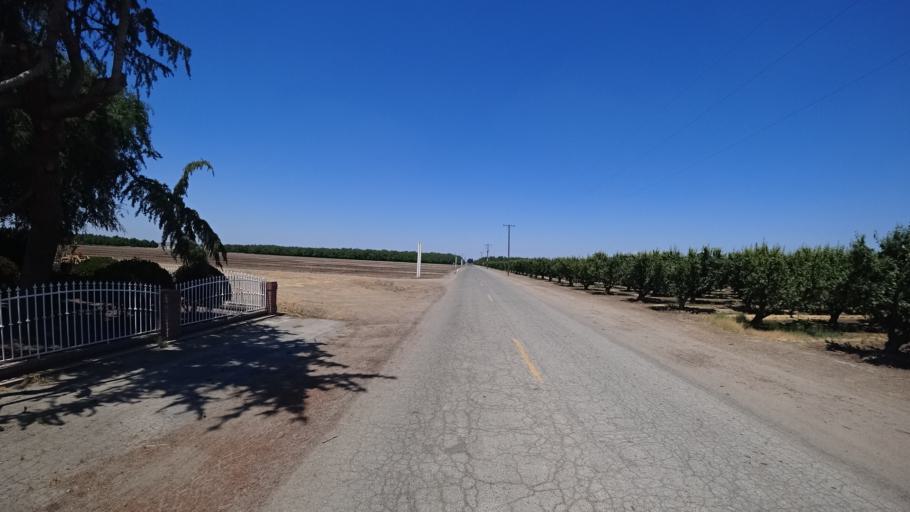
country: US
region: California
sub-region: Kings County
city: Lucerne
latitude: 36.3982
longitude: -119.6190
